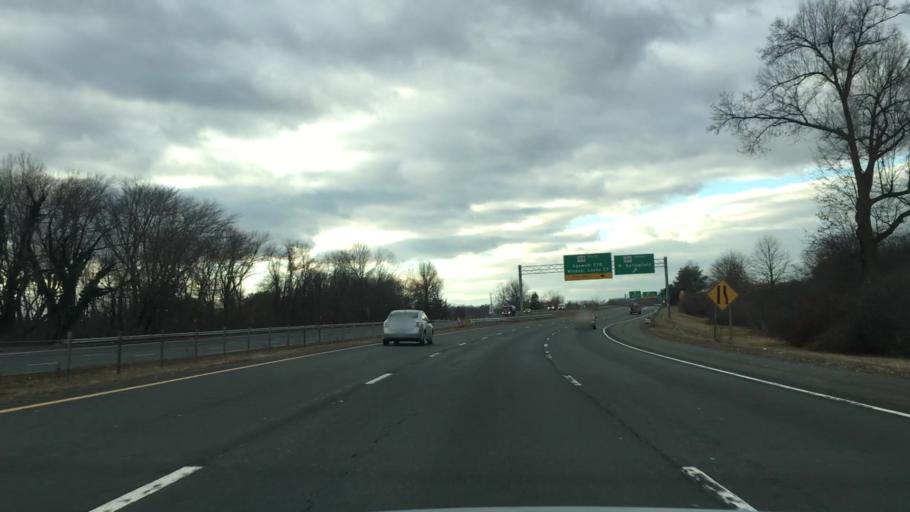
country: US
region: Massachusetts
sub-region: Hampden County
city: Agawam
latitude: 42.0760
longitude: -72.6099
